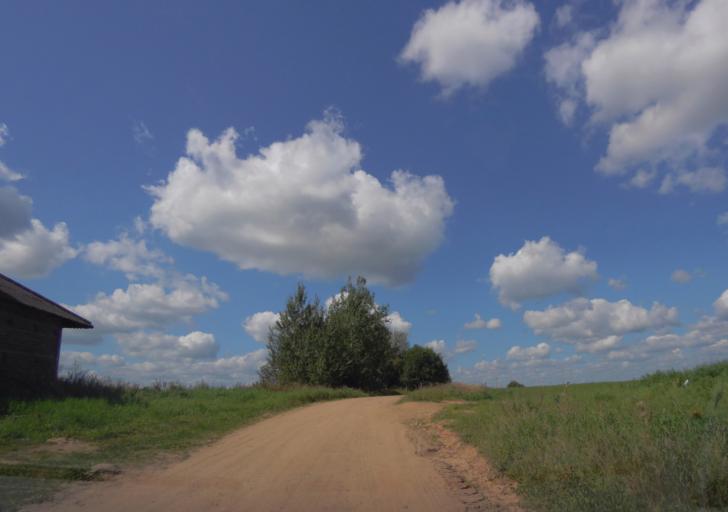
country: BY
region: Minsk
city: Horad Barysaw
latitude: 54.3643
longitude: 28.4659
